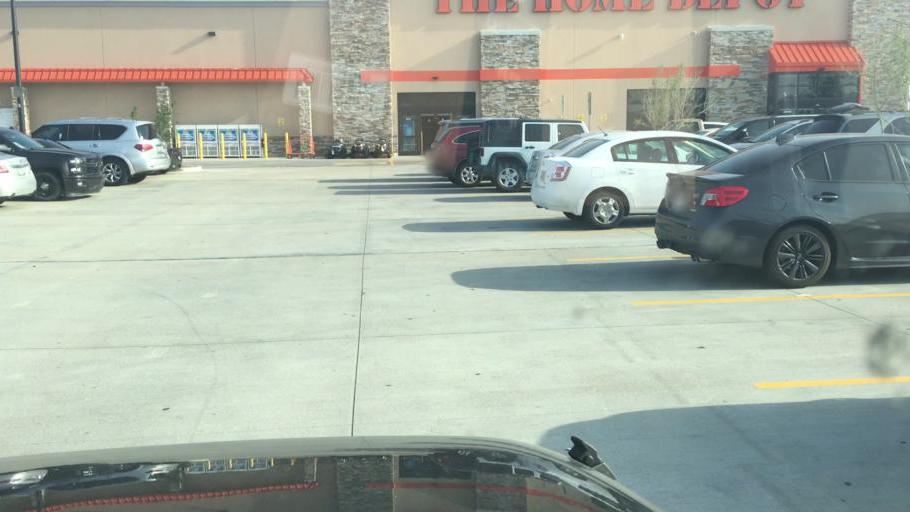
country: US
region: Texas
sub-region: Harris County
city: Atascocita
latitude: 29.9226
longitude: -95.1950
